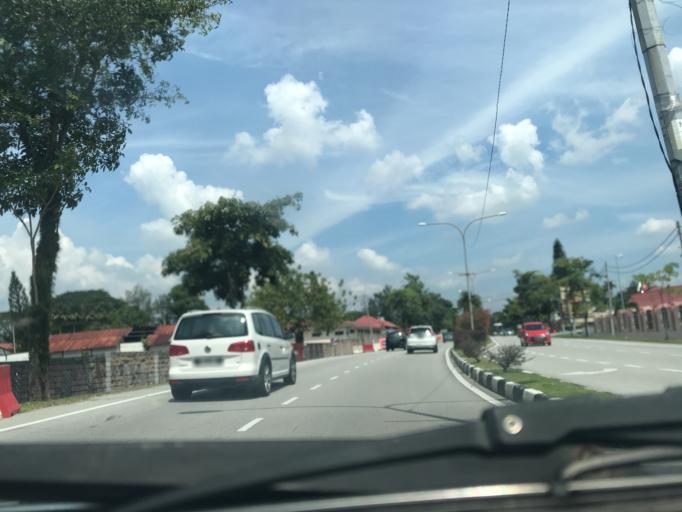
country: MY
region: Perak
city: Ipoh
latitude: 4.6011
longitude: 101.1045
